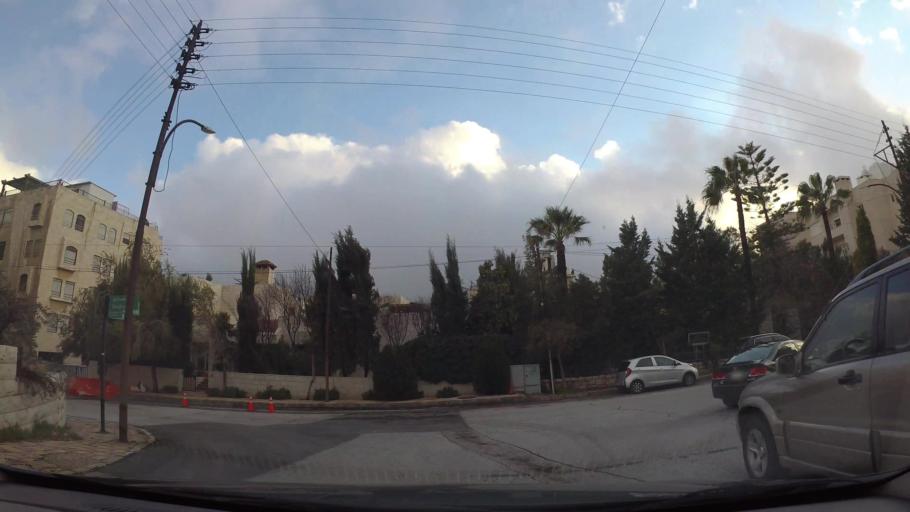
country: JO
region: Amman
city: Amman
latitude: 31.9552
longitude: 35.8915
